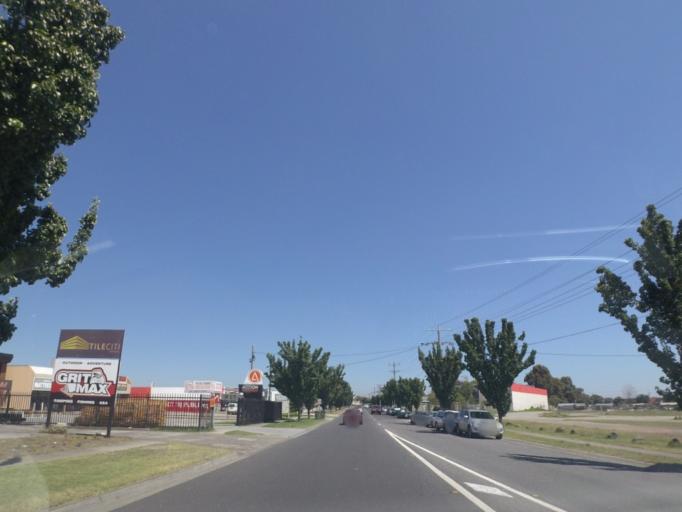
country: AU
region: Victoria
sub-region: Whittlesea
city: Thomastown
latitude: -37.6902
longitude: 145.0288
